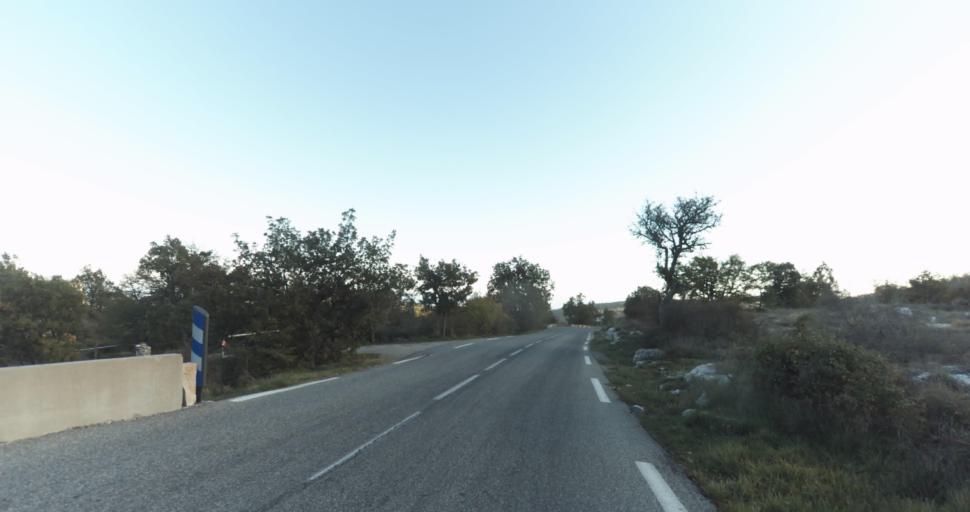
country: FR
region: Provence-Alpes-Cote d'Azur
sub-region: Departement des Alpes-Maritimes
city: Vence
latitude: 43.7632
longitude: 7.0852
